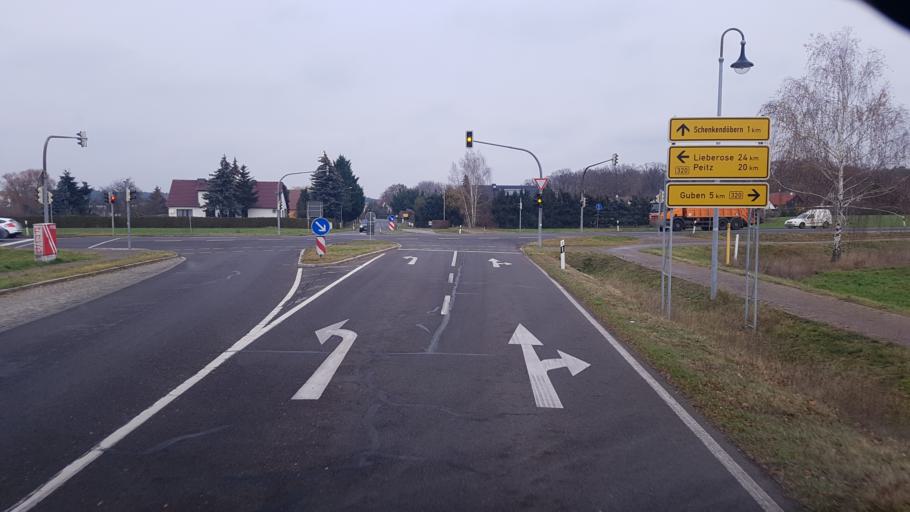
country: DE
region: Brandenburg
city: Schenkendobern
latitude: 51.9529
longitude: 14.6361
